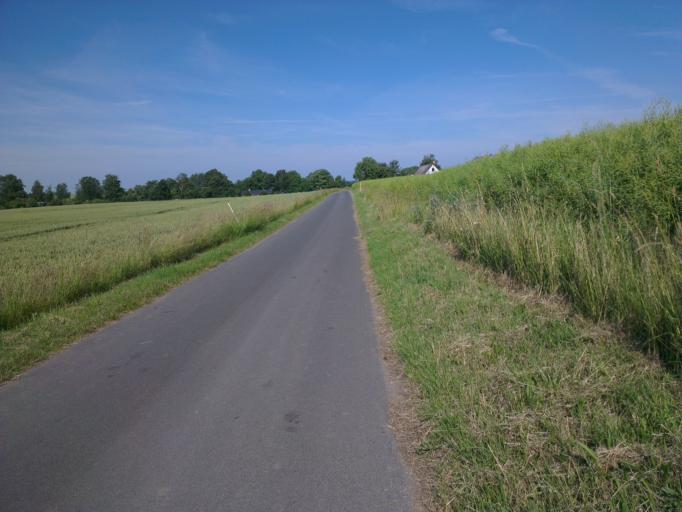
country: DK
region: Capital Region
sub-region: Frederikssund Kommune
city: Skibby
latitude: 55.7870
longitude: 11.8701
